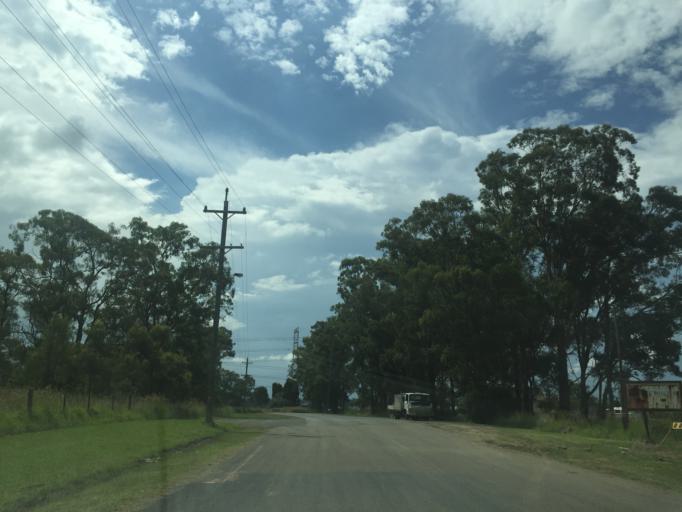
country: AU
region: New South Wales
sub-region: Blacktown
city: Blacktown
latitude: -33.8058
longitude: 150.9006
